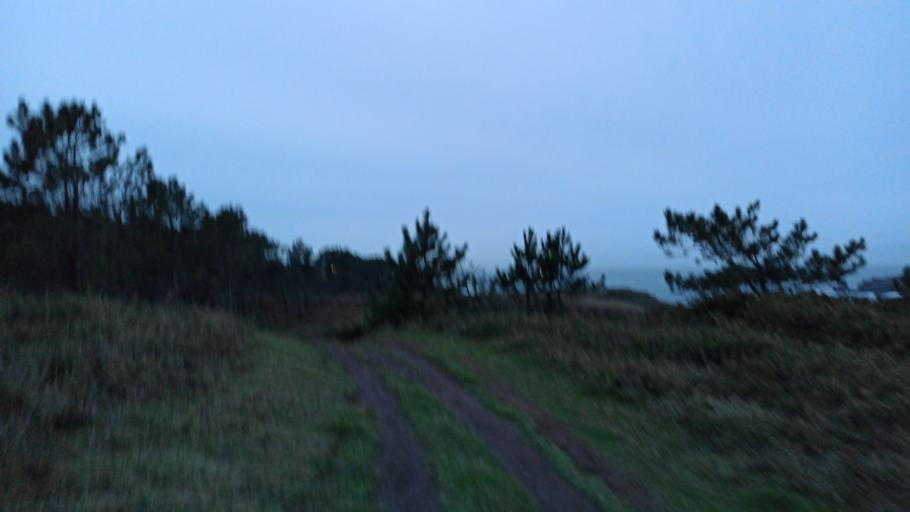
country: ES
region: Galicia
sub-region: Provincia da Coruna
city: Oleiros
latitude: 43.4022
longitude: -8.3239
